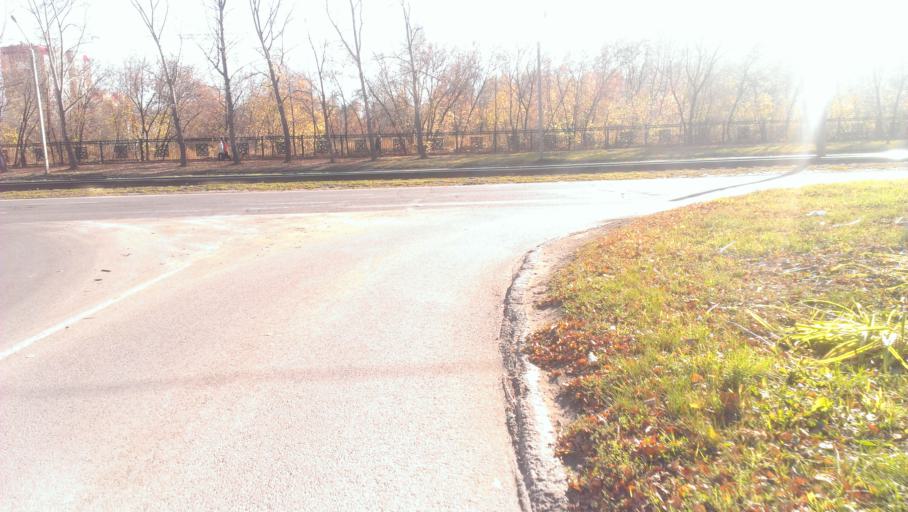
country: RU
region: Altai Krai
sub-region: Gorod Barnaulskiy
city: Barnaul
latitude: 53.3612
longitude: 83.6871
